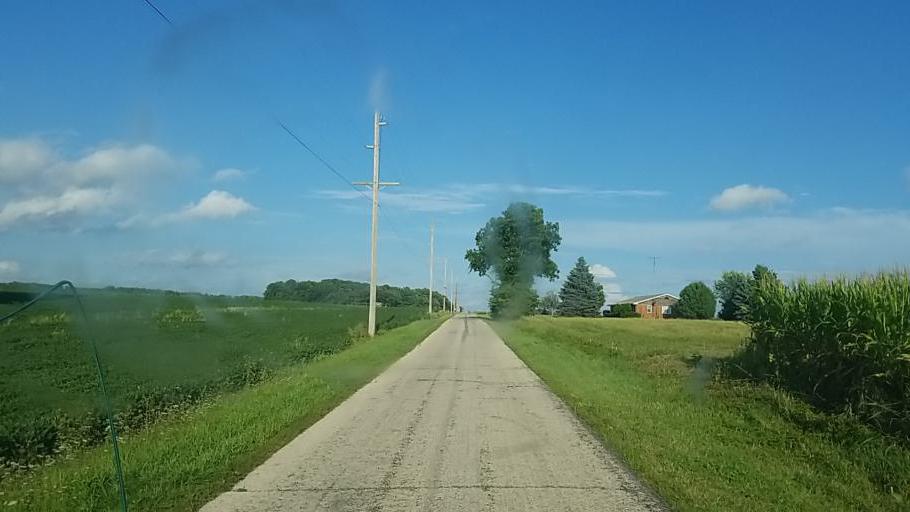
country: US
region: Ohio
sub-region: Crawford County
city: Bucyrus
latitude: 40.8338
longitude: -83.0973
